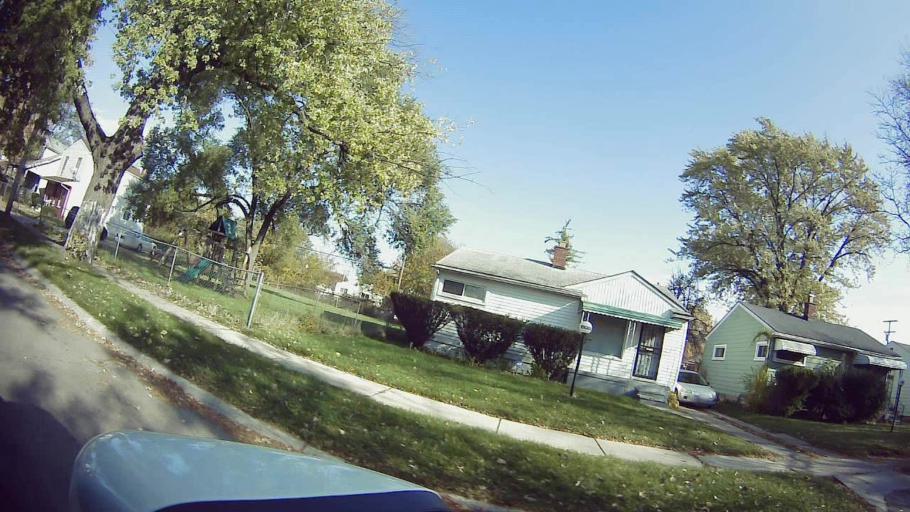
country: US
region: Michigan
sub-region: Wayne County
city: Hamtramck
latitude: 42.4272
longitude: -83.0617
